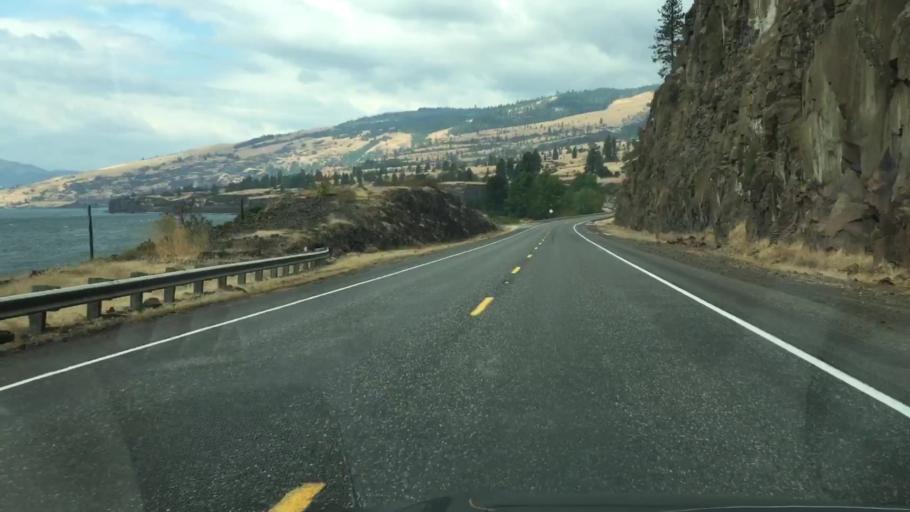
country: US
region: Oregon
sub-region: Wasco County
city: Chenoweth
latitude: 45.7089
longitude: -121.3376
